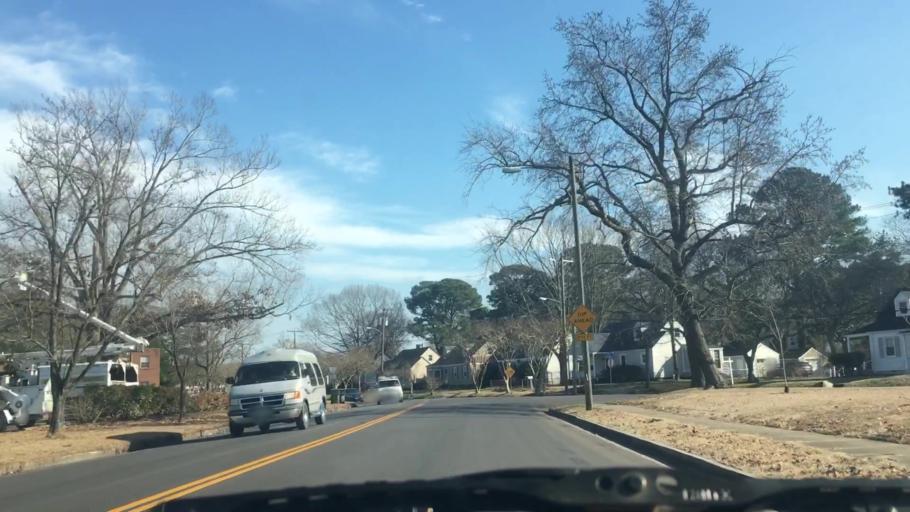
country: US
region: Virginia
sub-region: City of Norfolk
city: Norfolk
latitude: 36.8874
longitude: -76.2636
